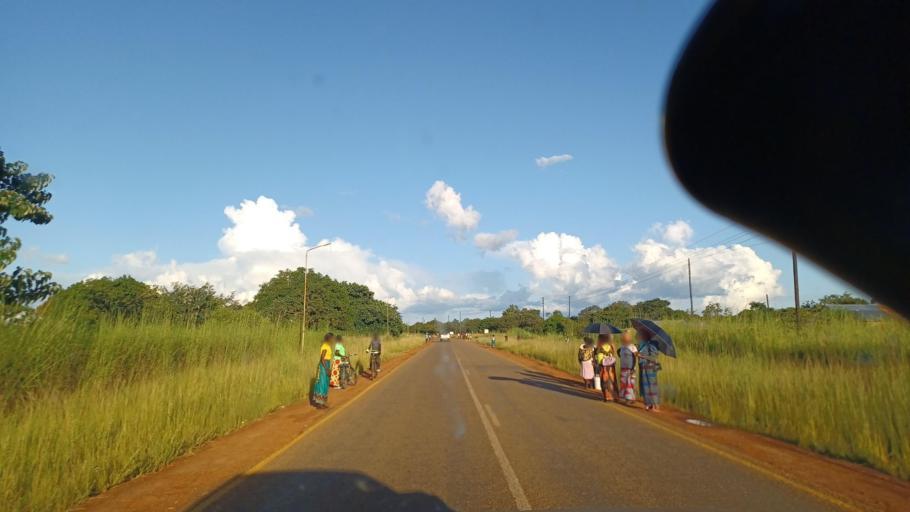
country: ZM
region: North-Western
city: Kalengwa
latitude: -13.1406
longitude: 25.0203
